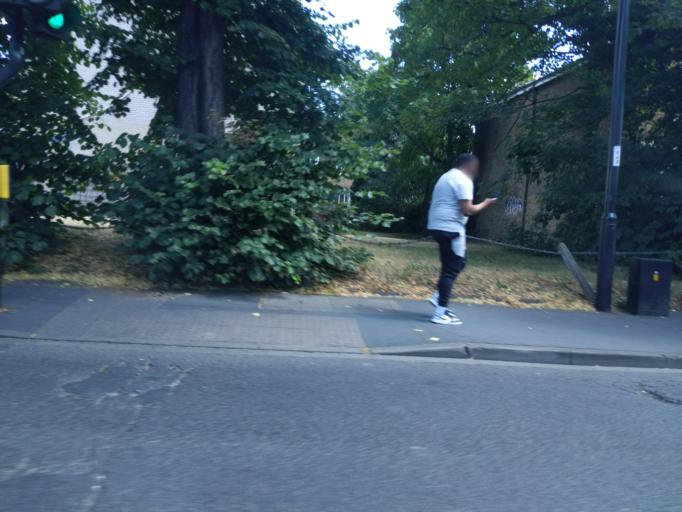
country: GB
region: England
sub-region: Greater London
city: Croydon
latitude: 51.3807
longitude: -0.0993
